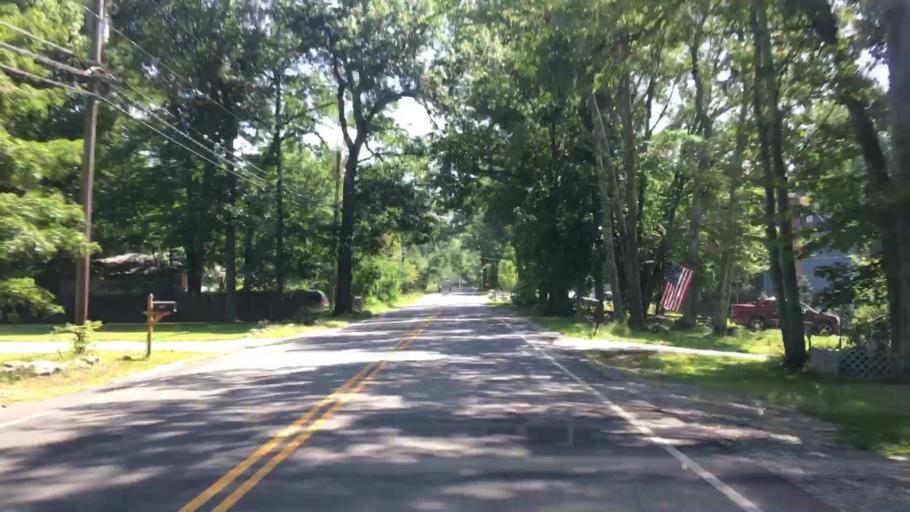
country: US
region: New Hampshire
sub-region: Rockingham County
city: Hampstead
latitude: 42.8572
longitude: -71.2204
